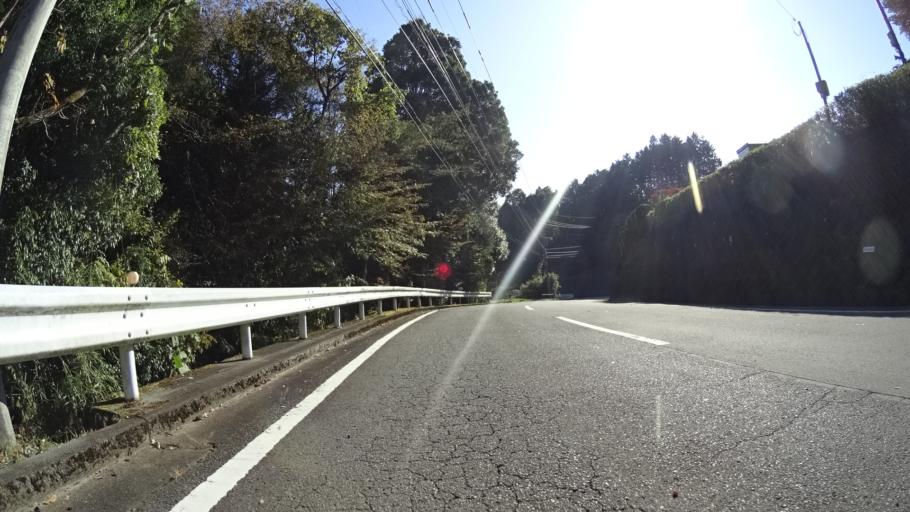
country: JP
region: Yamanashi
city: Uenohara
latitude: 35.6599
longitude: 139.1197
